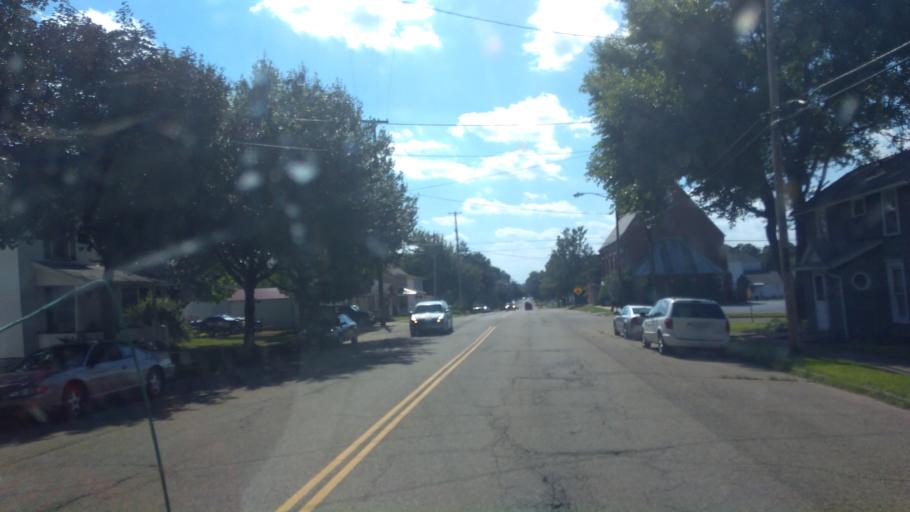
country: US
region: Ohio
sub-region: Stark County
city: Navarre
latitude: 40.7242
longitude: -81.5159
